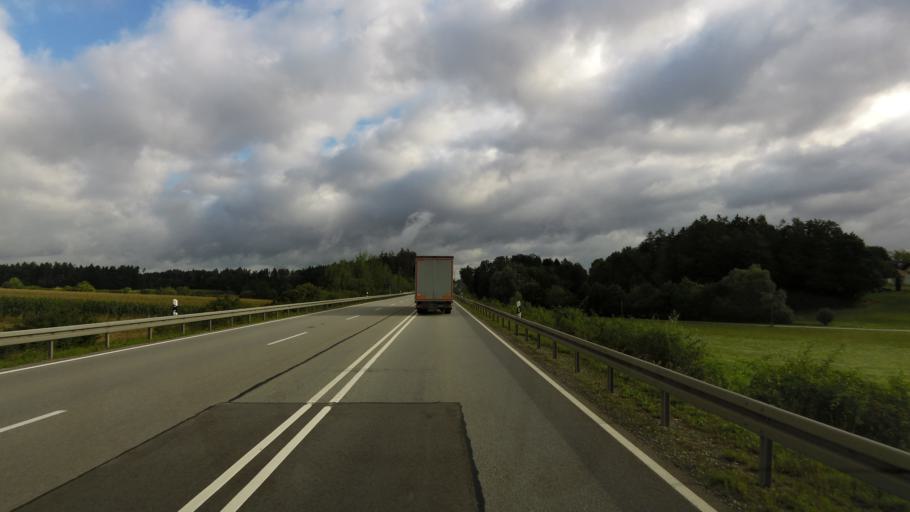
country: DE
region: Bavaria
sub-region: Lower Bavaria
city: Steinach
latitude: 48.9674
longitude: 12.6248
